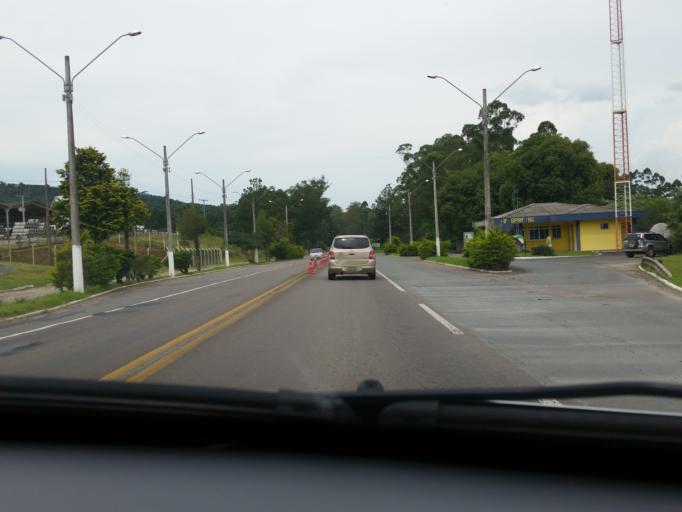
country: BR
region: Santa Catarina
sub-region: Rio Do Sul
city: Rio do Sul
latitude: -27.1723
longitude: -49.5819
